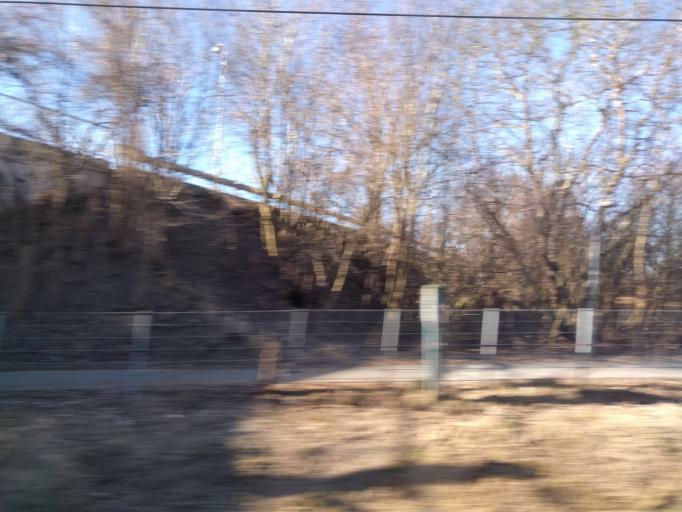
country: DK
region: Capital Region
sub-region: Horsholm Kommune
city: Horsholm
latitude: 55.8934
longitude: 12.5151
